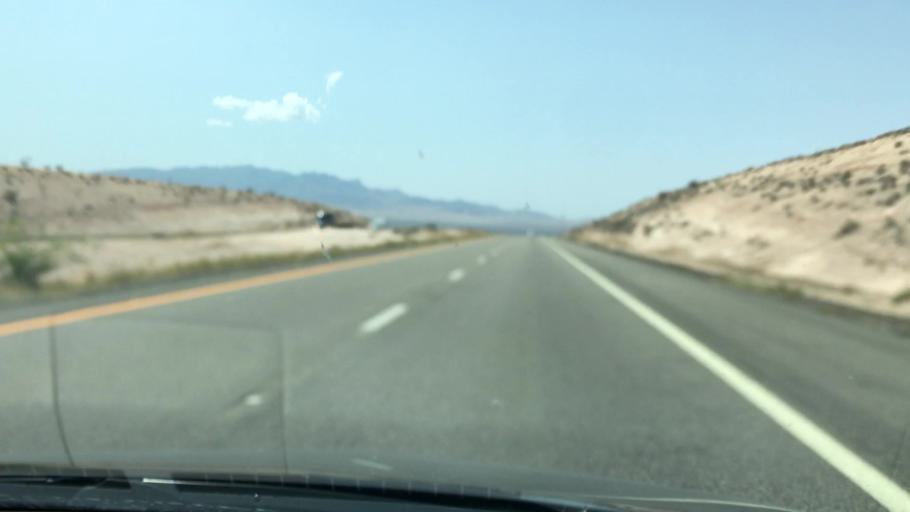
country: US
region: Nevada
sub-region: Clark County
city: Mesquite
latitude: 36.8421
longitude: -113.9966
